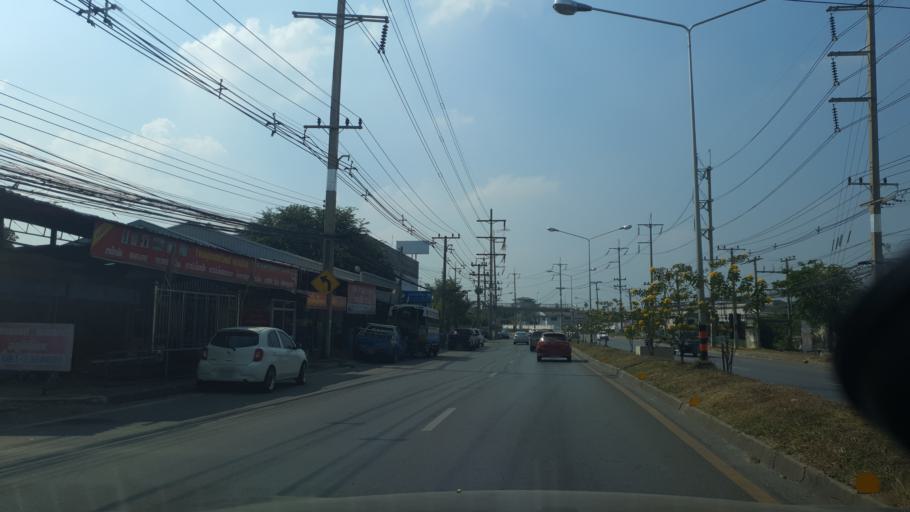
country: TH
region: Samut Sakhon
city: Krathum Baen
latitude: 13.6628
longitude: 100.2751
